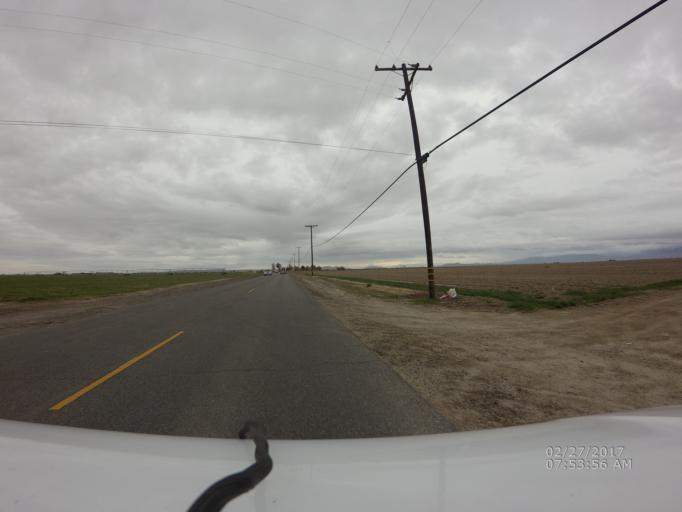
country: US
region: California
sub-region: Los Angeles County
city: Lancaster
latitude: 34.7045
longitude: -118.0323
